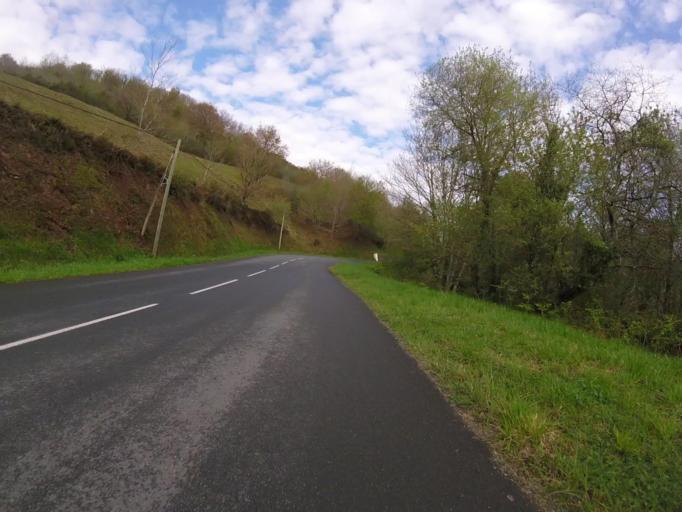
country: FR
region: Aquitaine
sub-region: Departement des Pyrenees-Atlantiques
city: Sare
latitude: 43.3161
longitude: -1.5943
